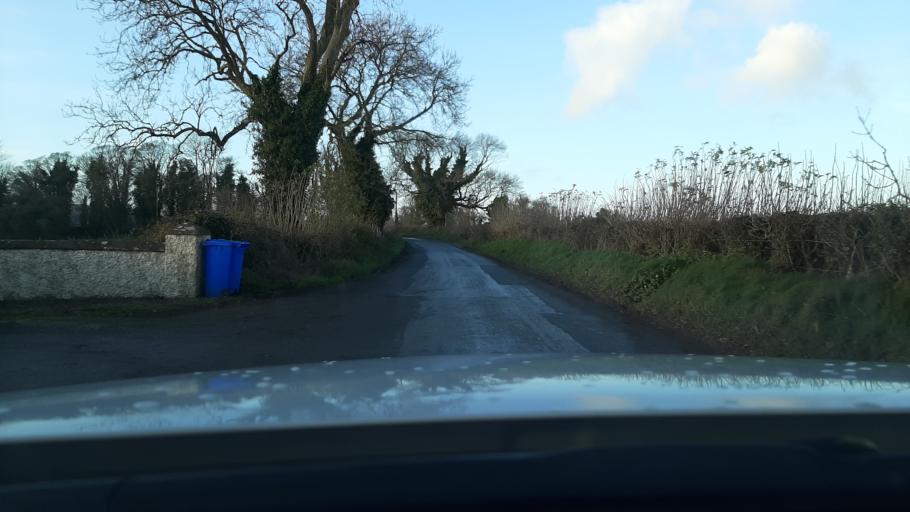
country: IE
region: Leinster
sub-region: Kildare
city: Kildare
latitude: 53.1671
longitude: -6.9233
